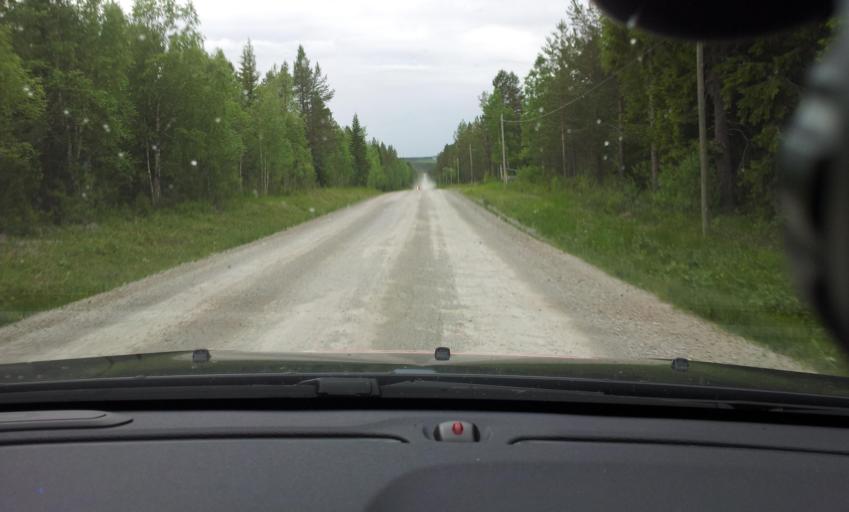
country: SE
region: Jaemtland
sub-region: OEstersunds Kommun
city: Brunflo
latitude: 63.0993
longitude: 14.9476
